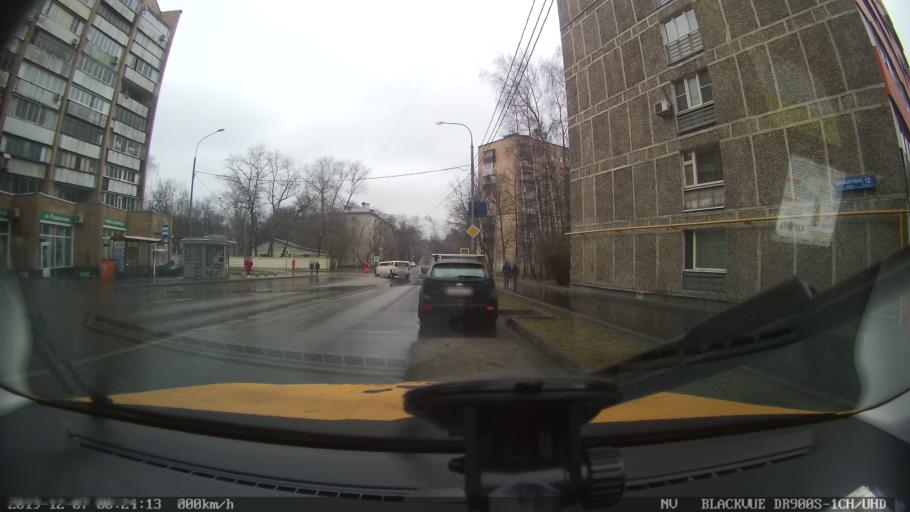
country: RU
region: Moscow
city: Rostokino
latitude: 55.8307
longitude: 37.6639
